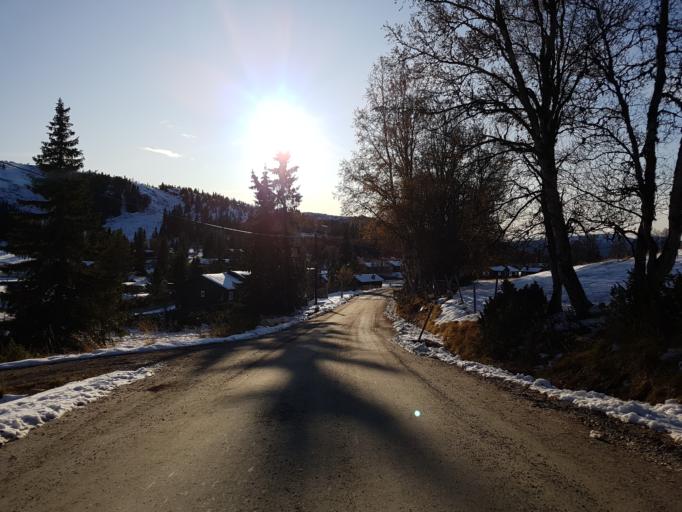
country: NO
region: Oppland
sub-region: Sel
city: Otta
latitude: 61.8095
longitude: 9.6871
